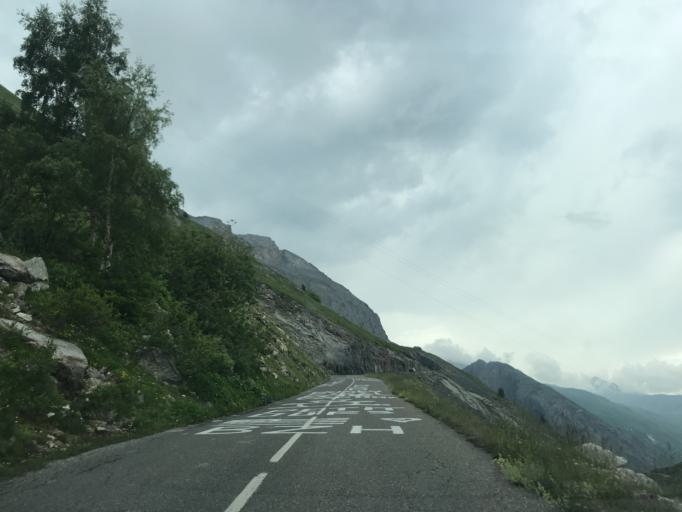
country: FR
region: Rhone-Alpes
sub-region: Departement de la Savoie
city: Valloire
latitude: 45.0862
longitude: 6.4357
